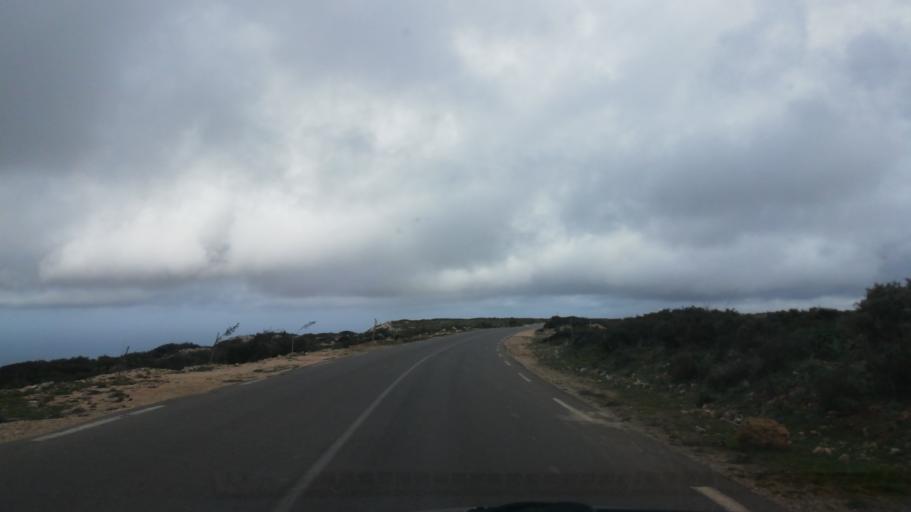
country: DZ
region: Oran
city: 'Ain el Turk
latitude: 35.6978
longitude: -0.7697
